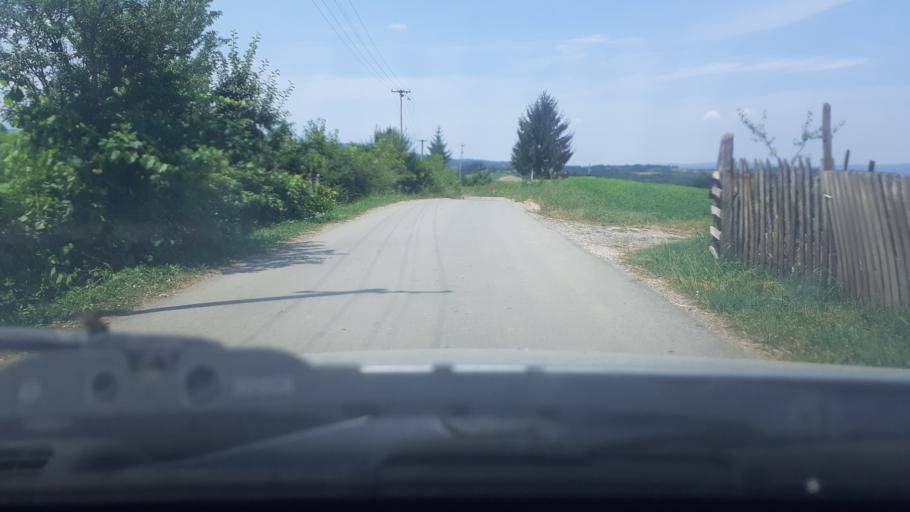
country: RS
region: Central Serbia
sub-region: Kolubarski Okrug
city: Osecina
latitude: 44.3926
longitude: 19.4949
